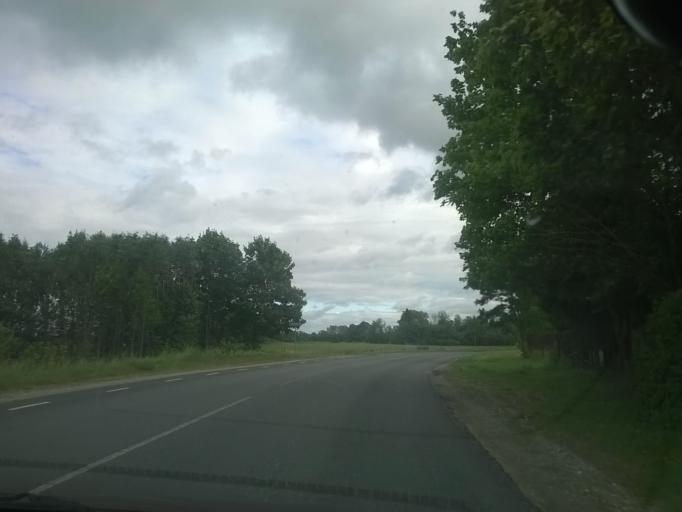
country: EE
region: Laeaene
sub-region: Ridala Parish
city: Uuemoisa
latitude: 58.9618
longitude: 23.7835
